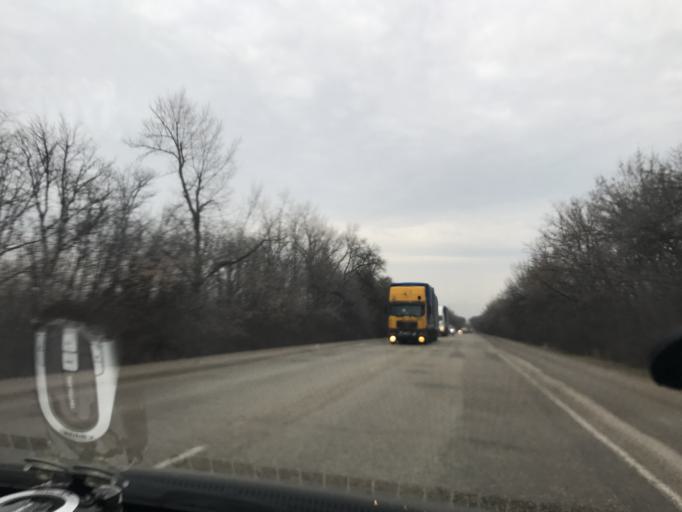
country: RU
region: Krasnodarskiy
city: Mirskoy
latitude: 45.5635
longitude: 40.4290
